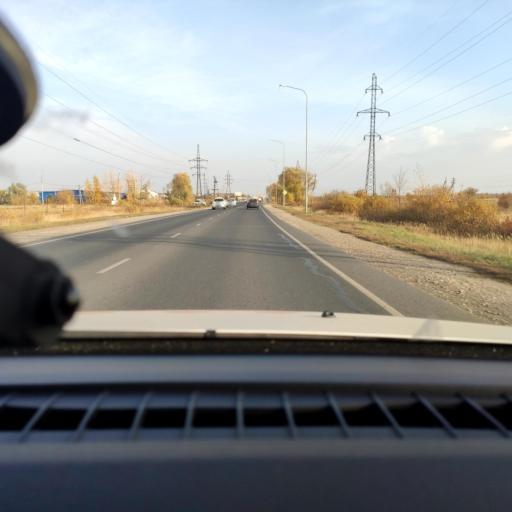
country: RU
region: Samara
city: Samara
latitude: 53.1310
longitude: 50.1458
